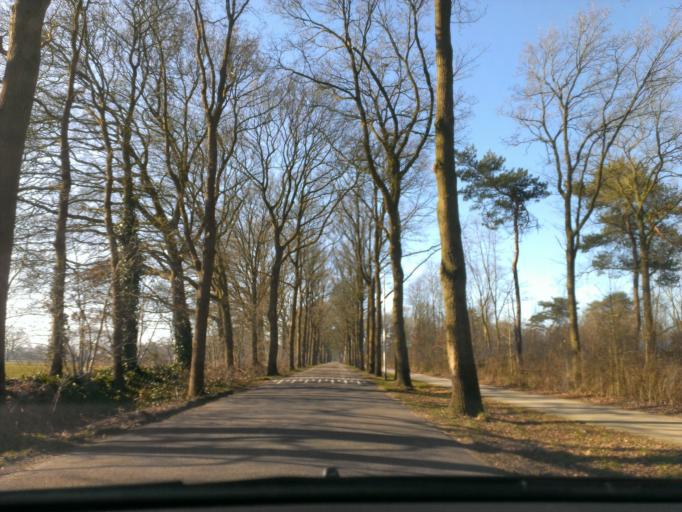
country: NL
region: Drenthe
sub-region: Gemeente De Wolden
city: Ruinen
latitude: 52.6992
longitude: 6.3774
